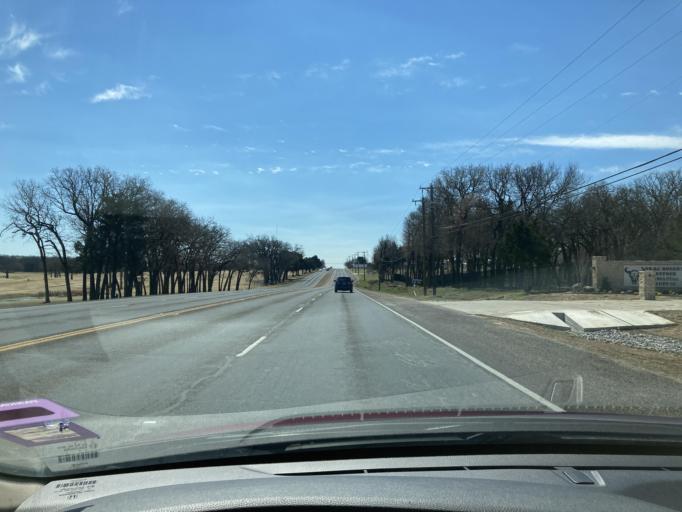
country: US
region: Texas
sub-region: Navarro County
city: Corsicana
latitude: 32.1200
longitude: -96.4652
